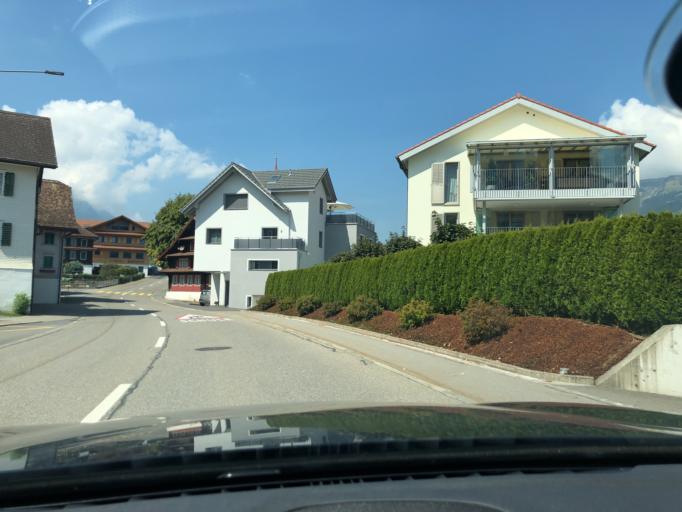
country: CH
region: Schwyz
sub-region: Bezirk Schwyz
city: Steinen
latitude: 47.0346
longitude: 8.5818
